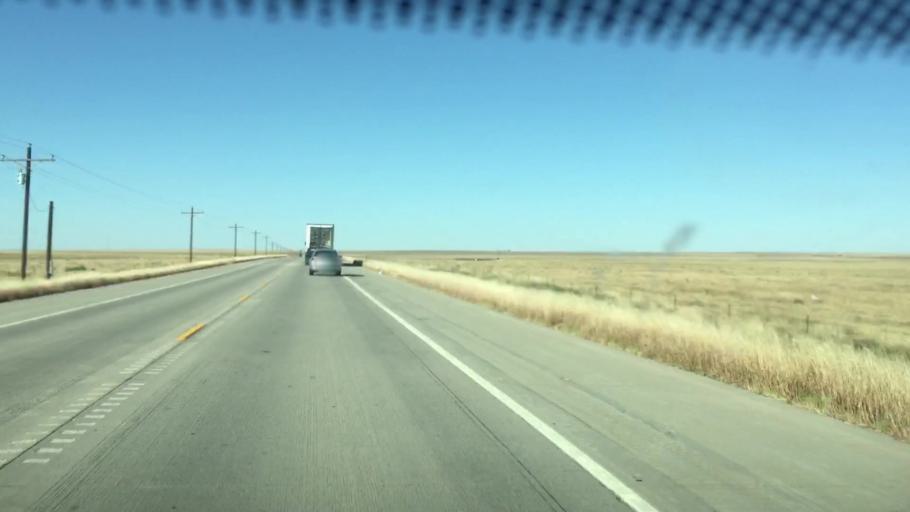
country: US
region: Colorado
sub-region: Kiowa County
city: Eads
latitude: 38.3792
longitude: -102.7302
